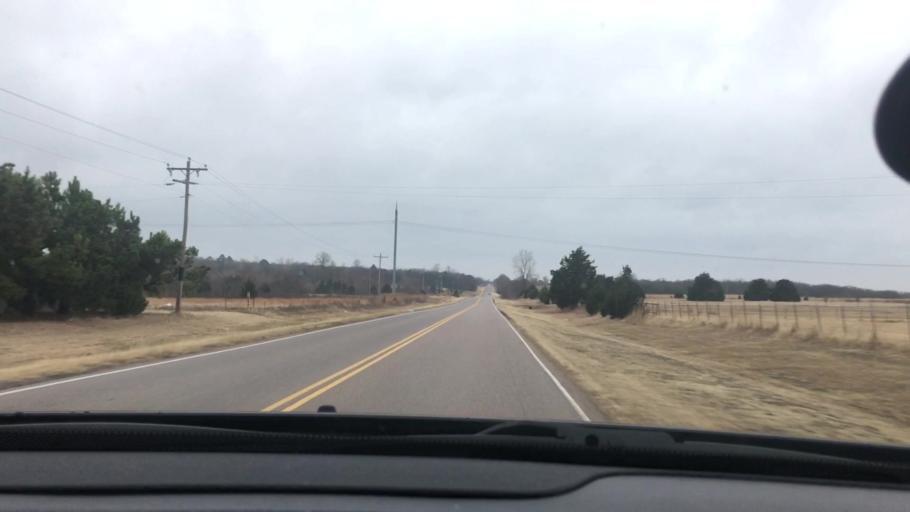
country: US
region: Oklahoma
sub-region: Johnston County
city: Tishomingo
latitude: 34.2697
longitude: -96.6711
